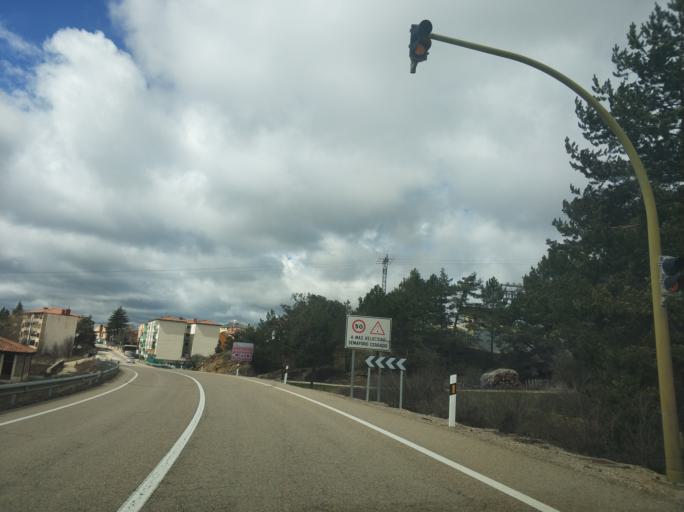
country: ES
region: Castille and Leon
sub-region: Provincia de Soria
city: Navaleno
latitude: 41.8356
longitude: -3.0008
